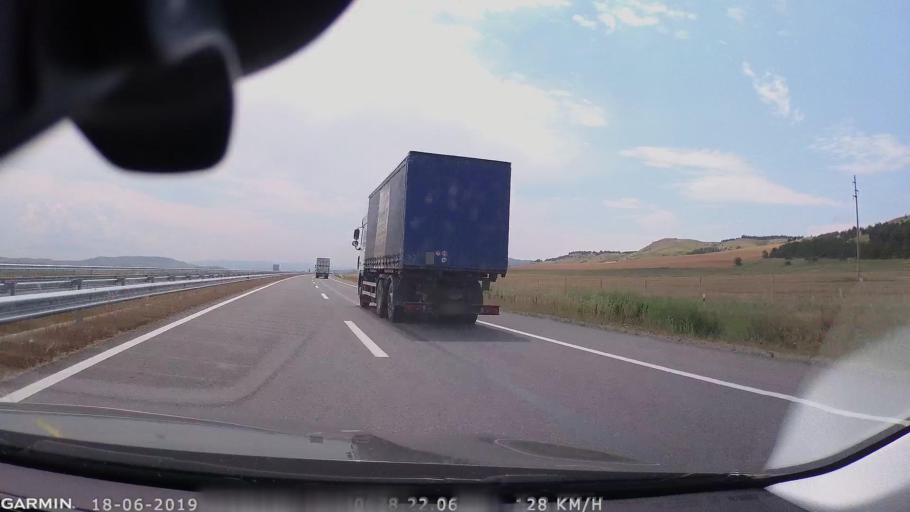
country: MK
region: Sveti Nikole
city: Sveti Nikole
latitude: 41.8064
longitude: 22.0658
